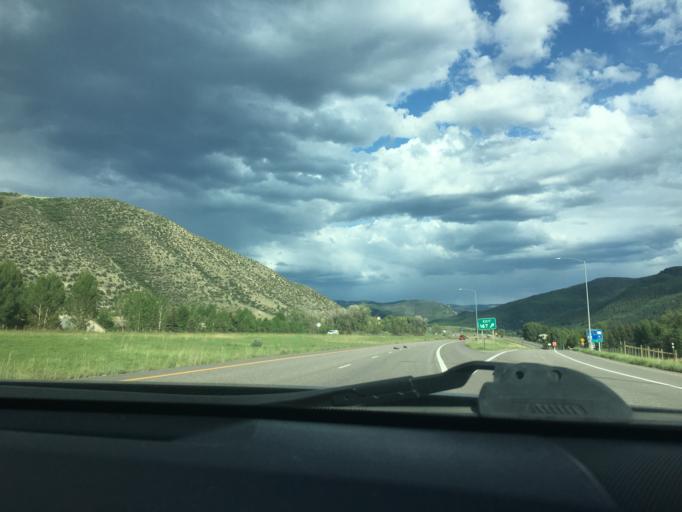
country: US
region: Colorado
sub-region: Eagle County
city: Avon
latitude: 39.6389
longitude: -106.5249
